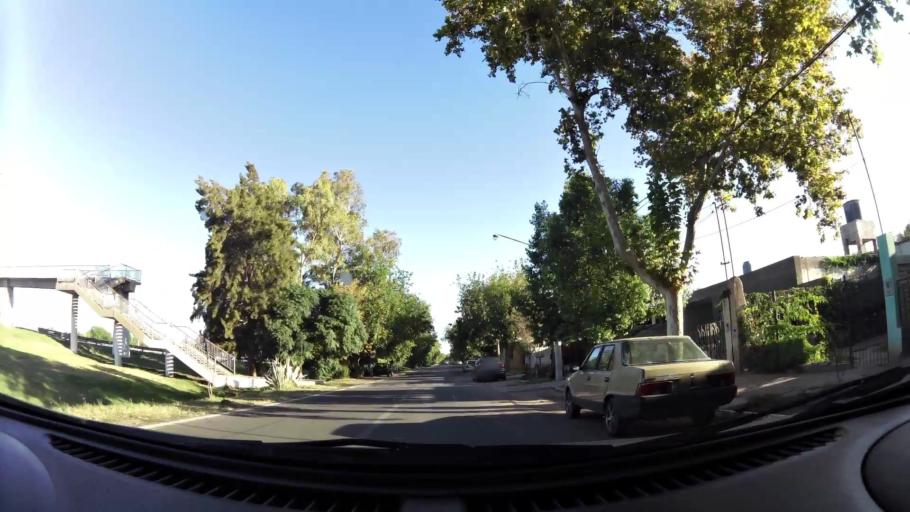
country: AR
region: San Juan
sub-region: Departamento de Santa Lucia
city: Santa Lucia
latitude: -31.5383
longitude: -68.5044
